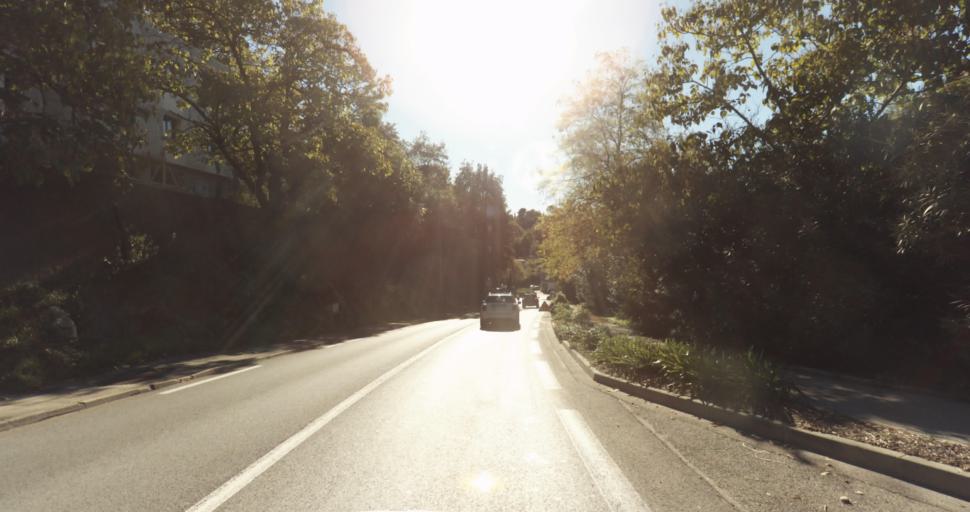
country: FR
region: Provence-Alpes-Cote d'Azur
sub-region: Departement des Alpes-Maritimes
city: Vence
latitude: 43.7188
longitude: 7.1136
